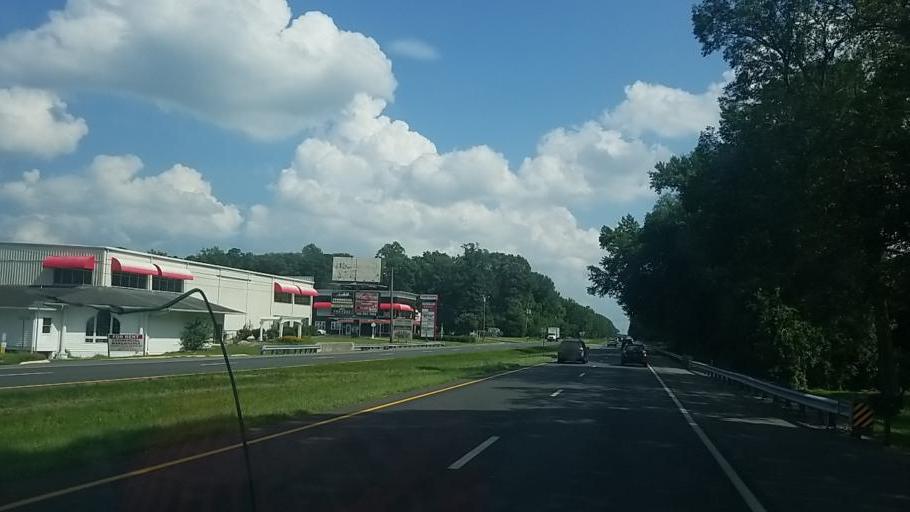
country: US
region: Delaware
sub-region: Sussex County
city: Millsboro
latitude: 38.5623
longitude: -75.2751
